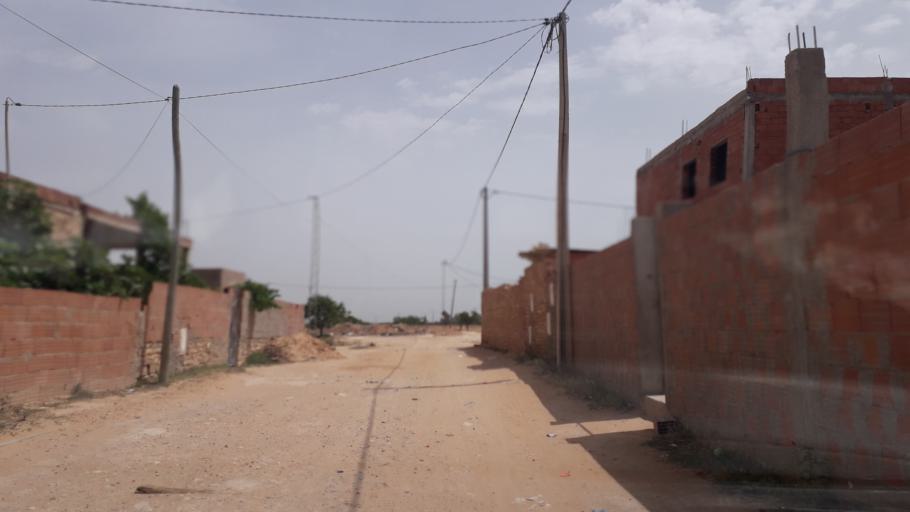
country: TN
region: Safaqis
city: Al Qarmadah
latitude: 34.8439
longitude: 10.7794
